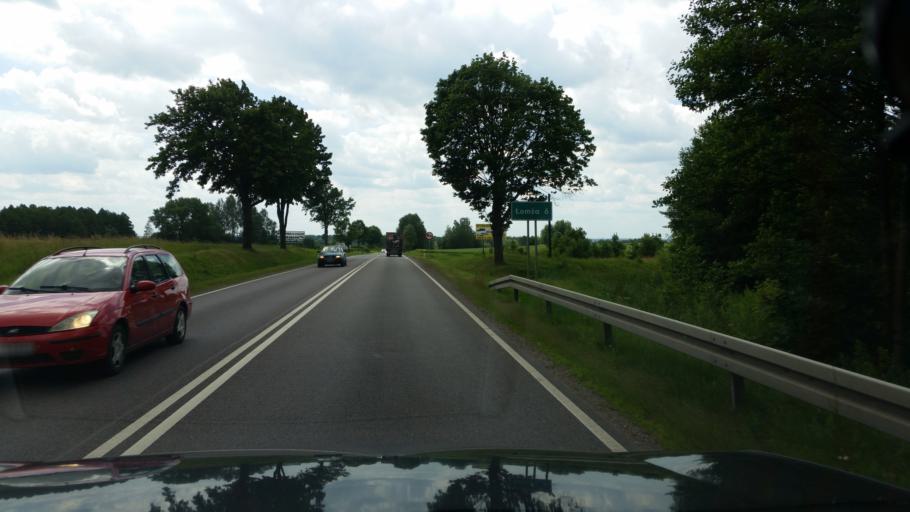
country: PL
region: Podlasie
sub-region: Powiat lomzynski
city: Piatnica
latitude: 53.2266
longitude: 22.1105
